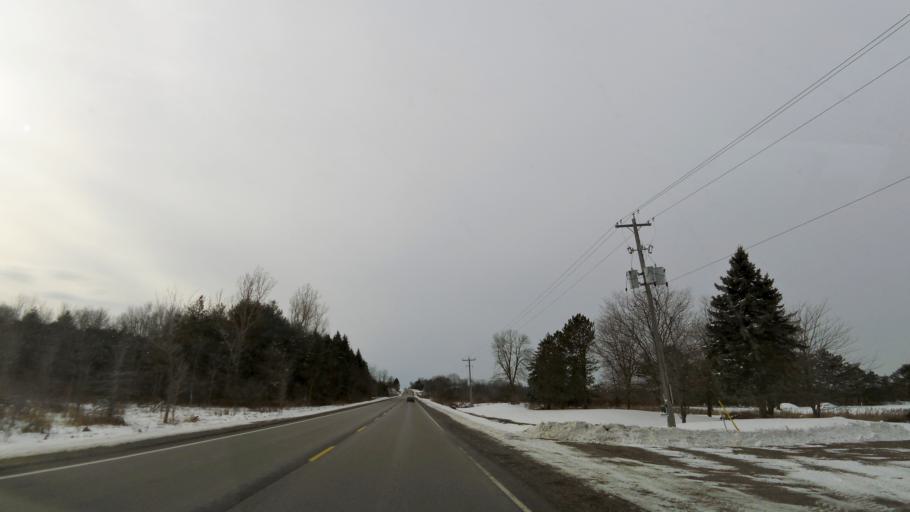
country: CA
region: Ontario
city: Ancaster
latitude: 43.2840
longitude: -80.0465
